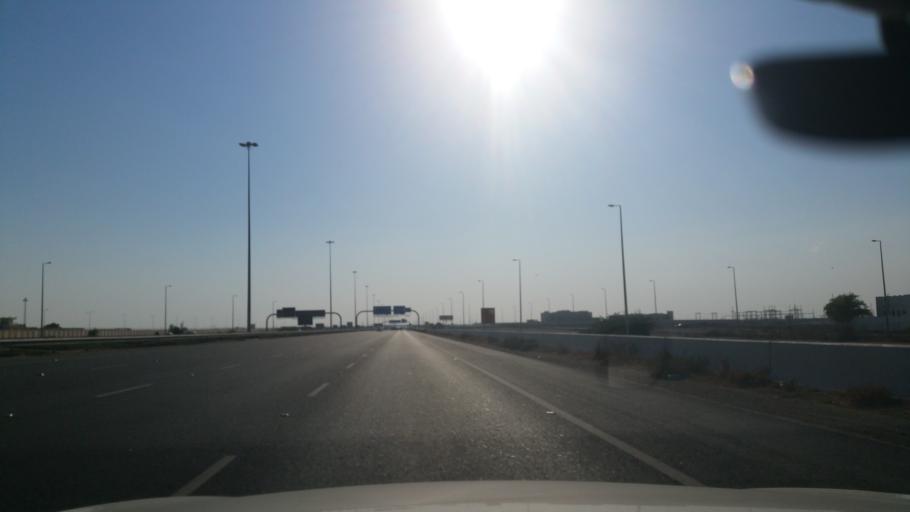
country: QA
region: Baladiyat ar Rayyan
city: Ar Rayyan
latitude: 25.2087
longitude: 51.4024
